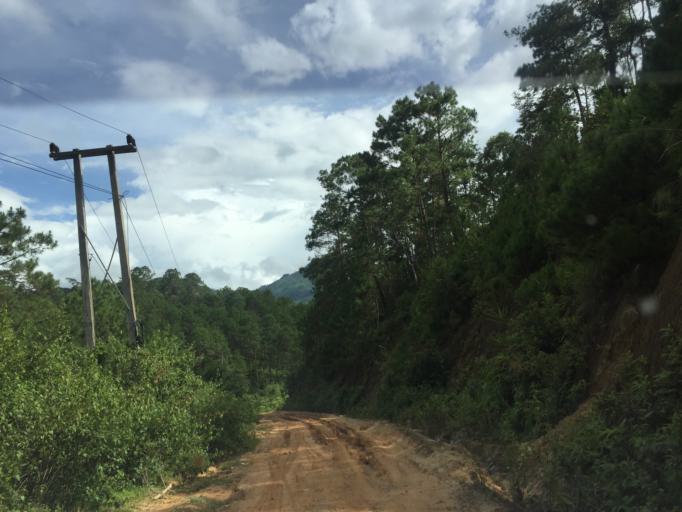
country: LA
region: Xiangkhoang
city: Muang Phonsavan
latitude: 19.3314
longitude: 103.4751
